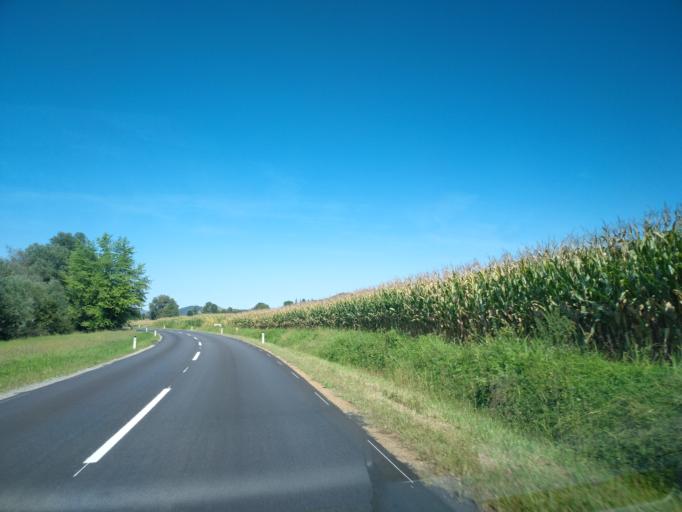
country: AT
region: Styria
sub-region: Politischer Bezirk Leibnitz
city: Sankt Johann im Saggautal
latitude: 46.7144
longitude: 15.4045
